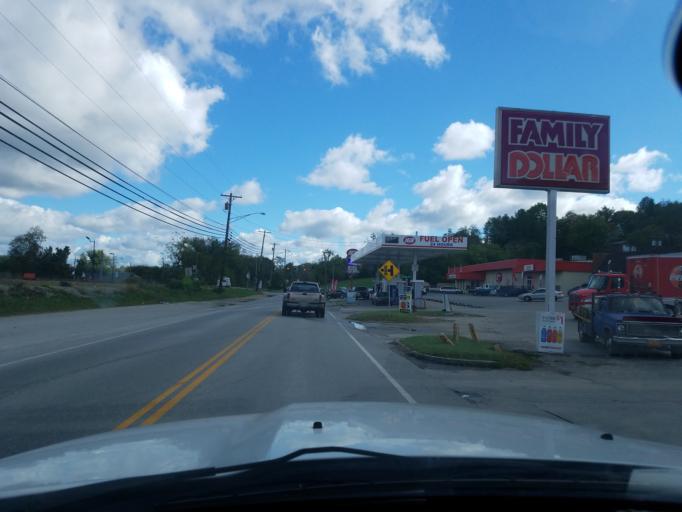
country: US
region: Kentucky
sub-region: Rockcastle County
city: Mount Vernon
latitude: 37.3519
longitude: -84.3467
